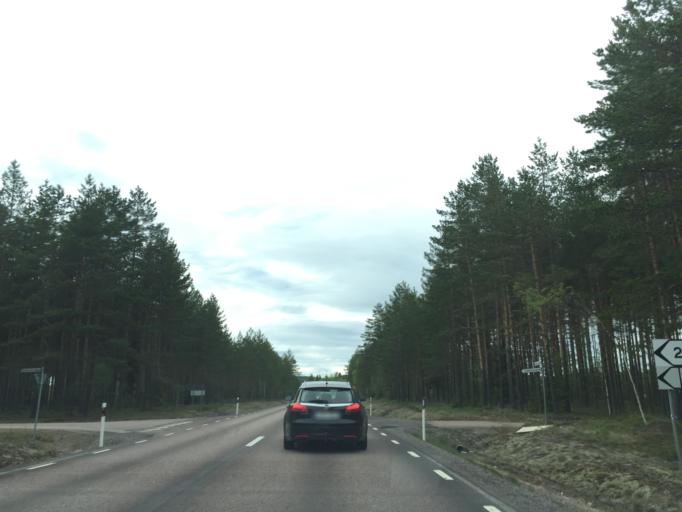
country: SE
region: Vaermland
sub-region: Eda Kommun
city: Charlottenberg
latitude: 59.9115
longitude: 12.2748
